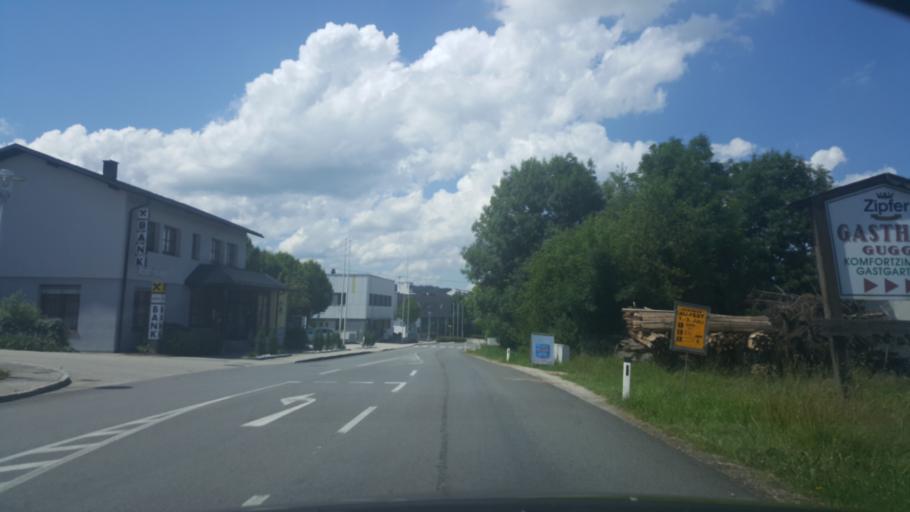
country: AT
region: Upper Austria
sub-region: Politischer Bezirk Vocklabruck
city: Gampern
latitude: 47.9881
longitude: 13.5541
